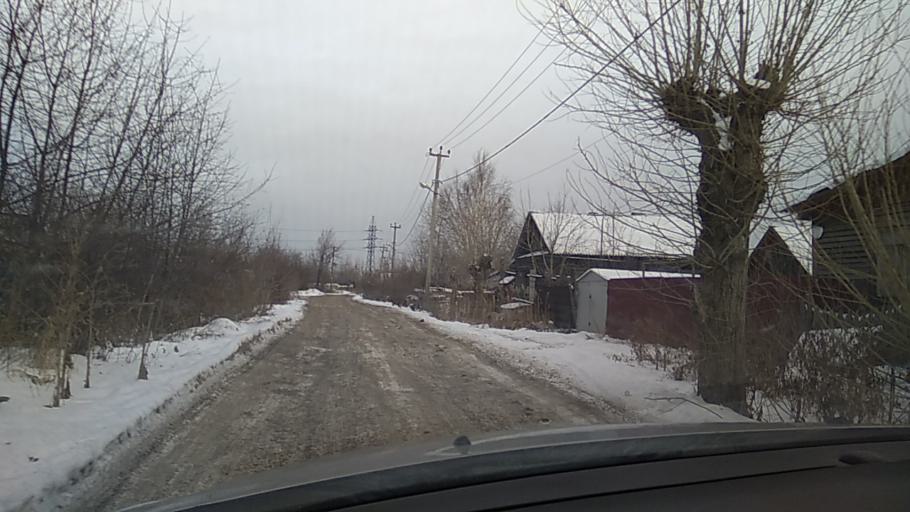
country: RU
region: Sverdlovsk
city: Shirokaya Rechka
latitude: 56.8332
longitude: 60.5279
